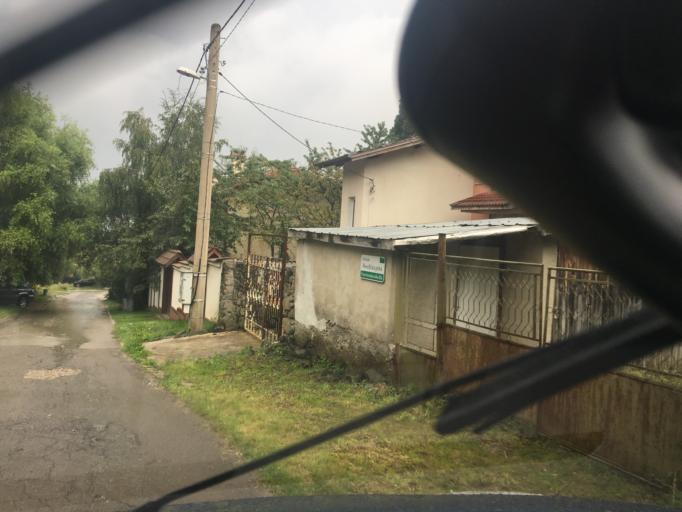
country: BG
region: Sofia-Capital
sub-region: Stolichna Obshtina
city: Sofia
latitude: 42.5863
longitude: 23.3466
